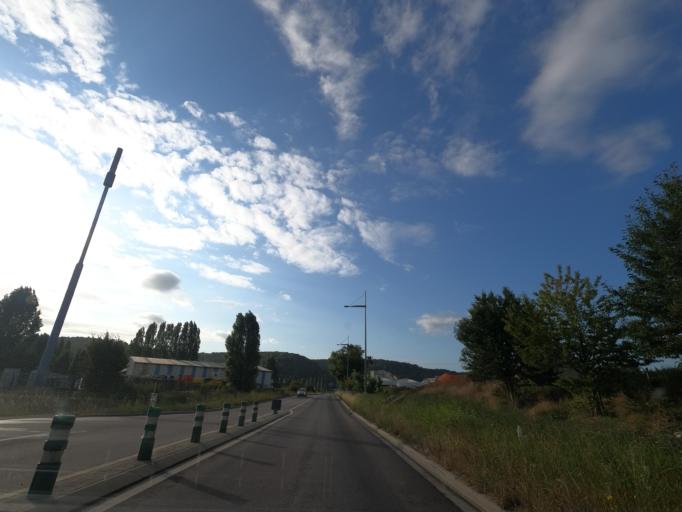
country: FR
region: Haute-Normandie
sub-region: Departement de la Seine-Maritime
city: Petit-Couronne
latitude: 49.4007
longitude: 1.0192
